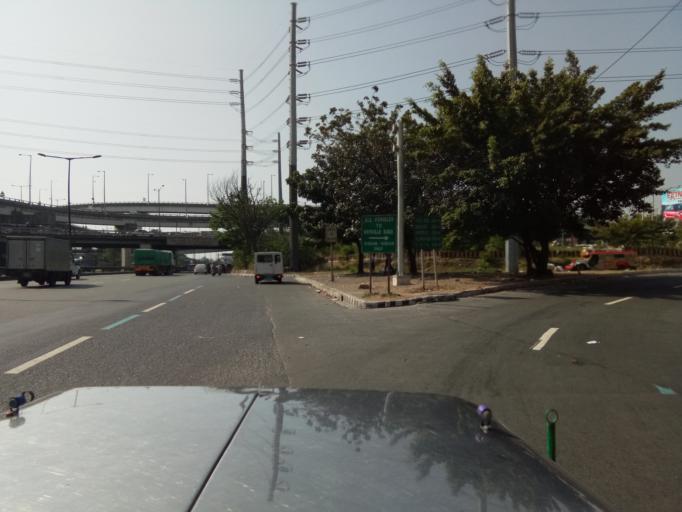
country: PH
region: Metro Manila
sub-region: Makati City
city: Makati City
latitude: 14.5251
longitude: 121.0249
